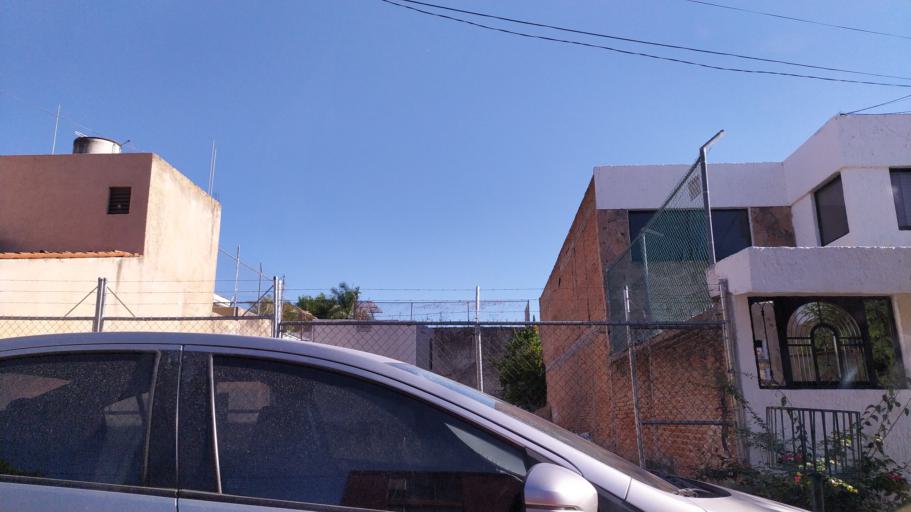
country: MX
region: Jalisco
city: Guadalajara
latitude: 20.6579
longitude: -103.4256
